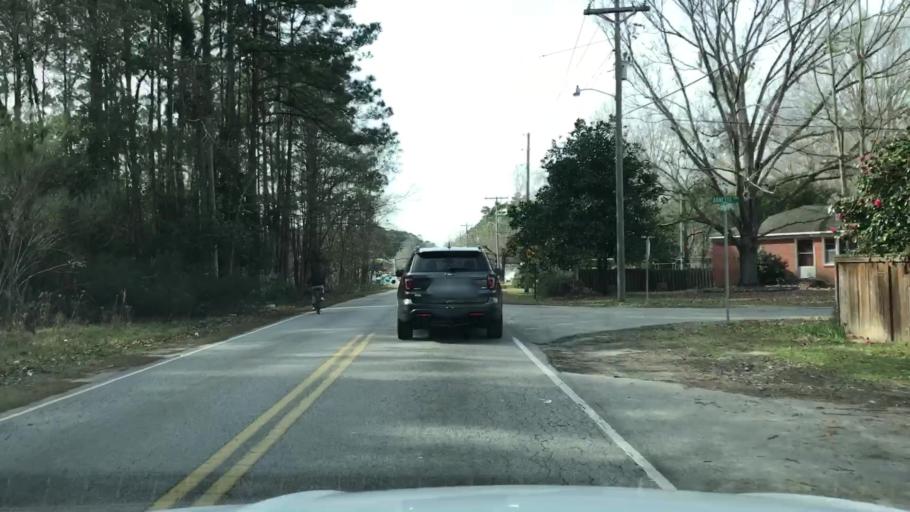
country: US
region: South Carolina
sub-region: Berkeley County
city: Goose Creek
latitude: 33.0180
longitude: -80.0329
